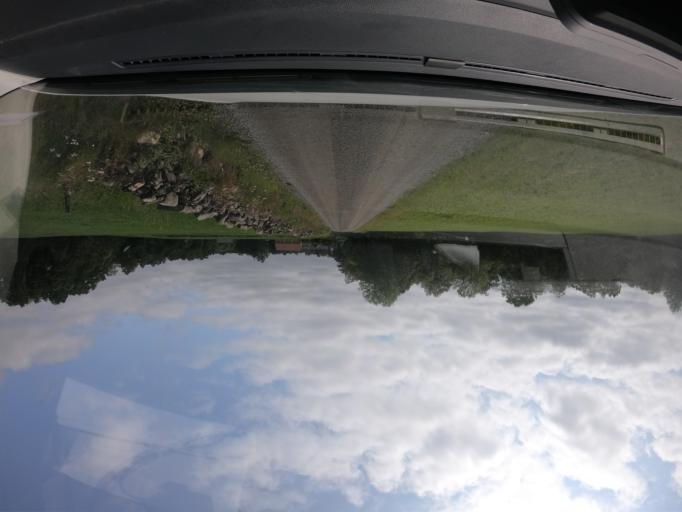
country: SE
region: Skane
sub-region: Hassleholms Kommun
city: Sosdala
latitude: 56.1223
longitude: 13.6003
